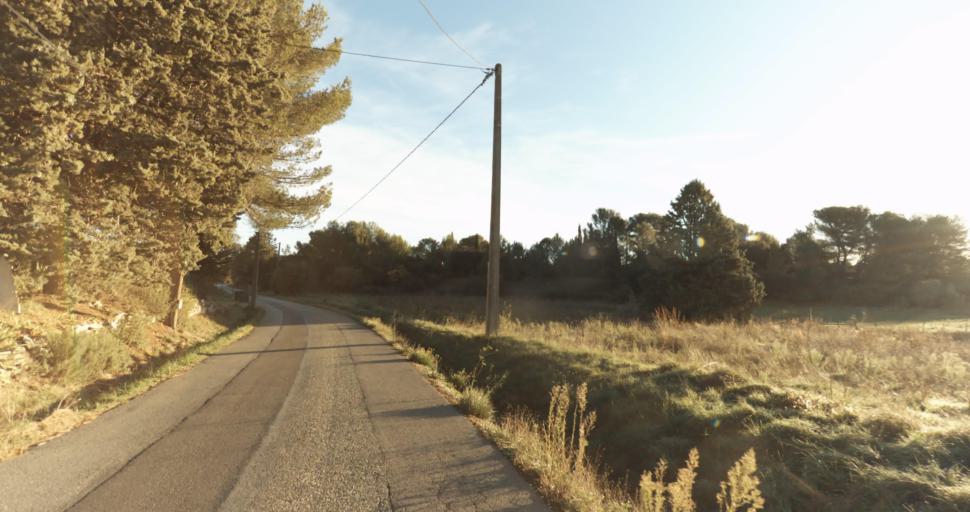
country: FR
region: Provence-Alpes-Cote d'Azur
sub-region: Departement des Bouches-du-Rhone
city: Venelles
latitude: 43.5801
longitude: 5.4983
